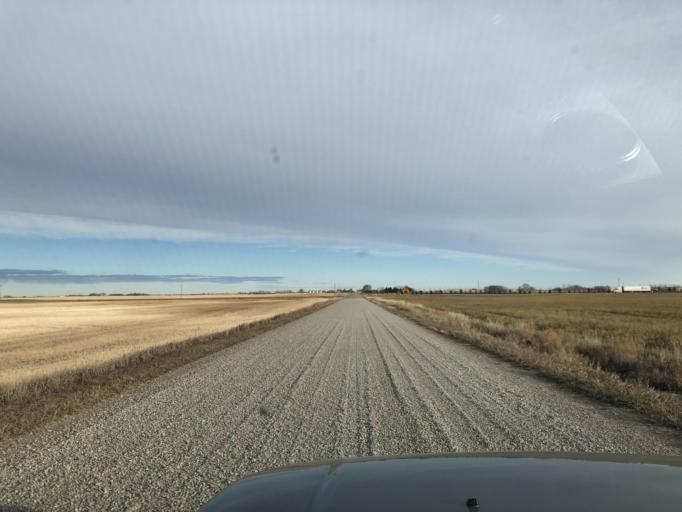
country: CA
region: Alberta
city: Strathmore
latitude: 50.8926
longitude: -113.5418
